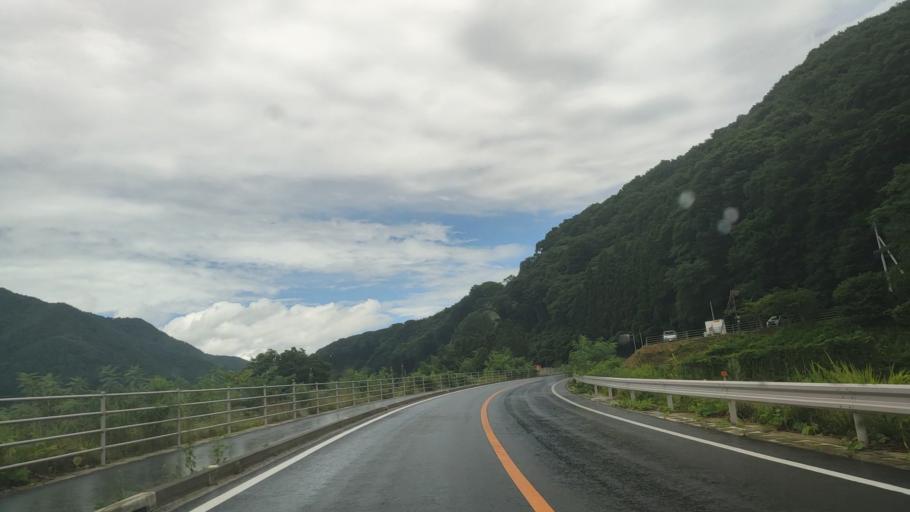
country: JP
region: Gunma
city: Numata
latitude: 36.7606
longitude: 139.2282
